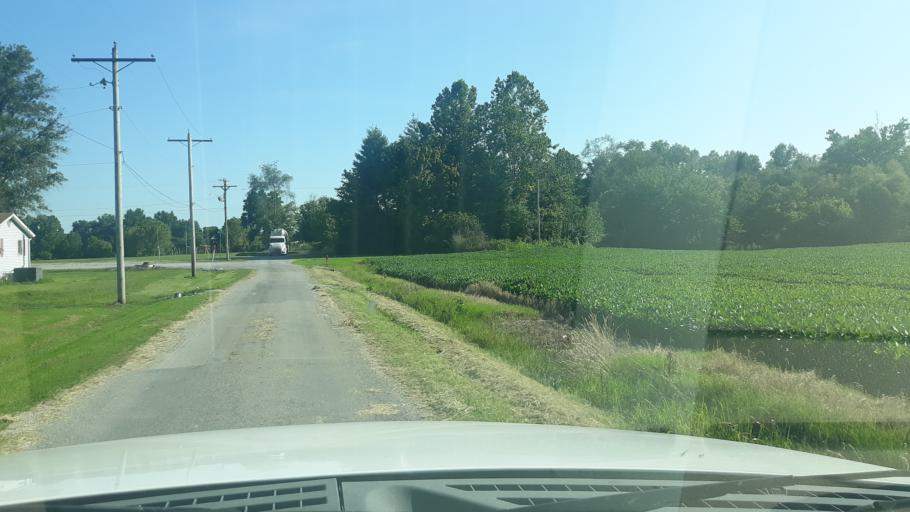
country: US
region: Illinois
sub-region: Saline County
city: Harrisburg
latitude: 37.8397
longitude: -88.6160
